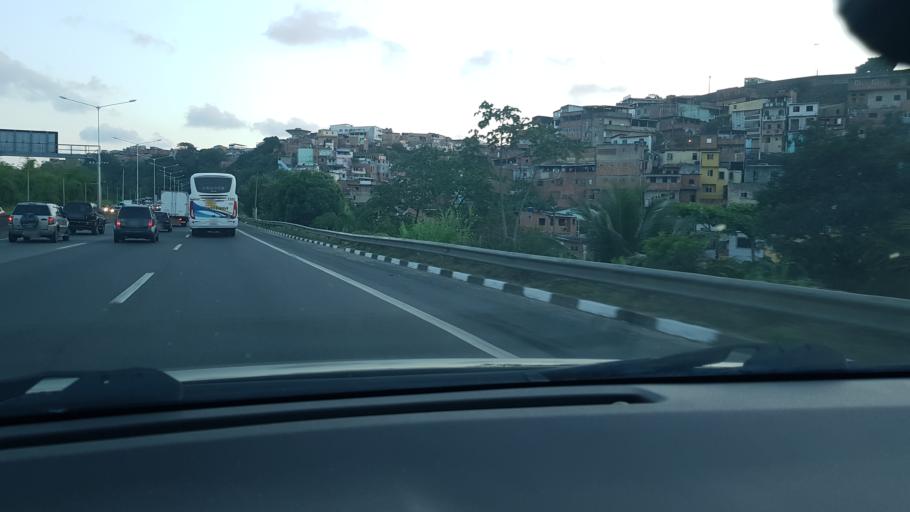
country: BR
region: Bahia
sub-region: Salvador
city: Salvador
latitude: -12.9320
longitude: -38.4713
